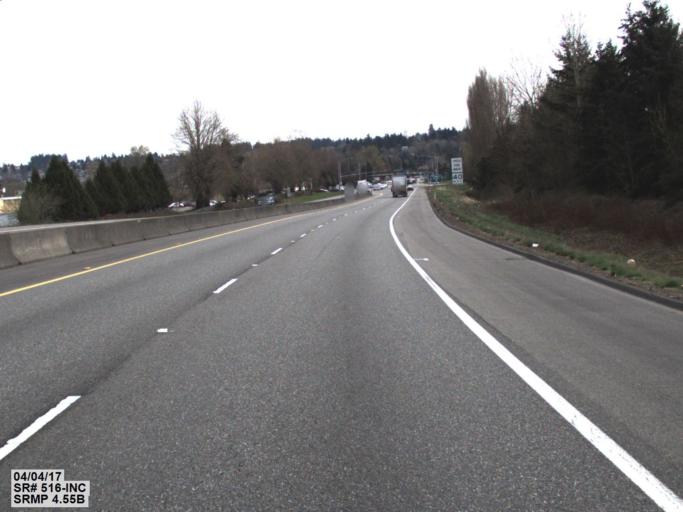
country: US
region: Washington
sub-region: King County
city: Kent
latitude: 47.3779
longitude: -122.2526
